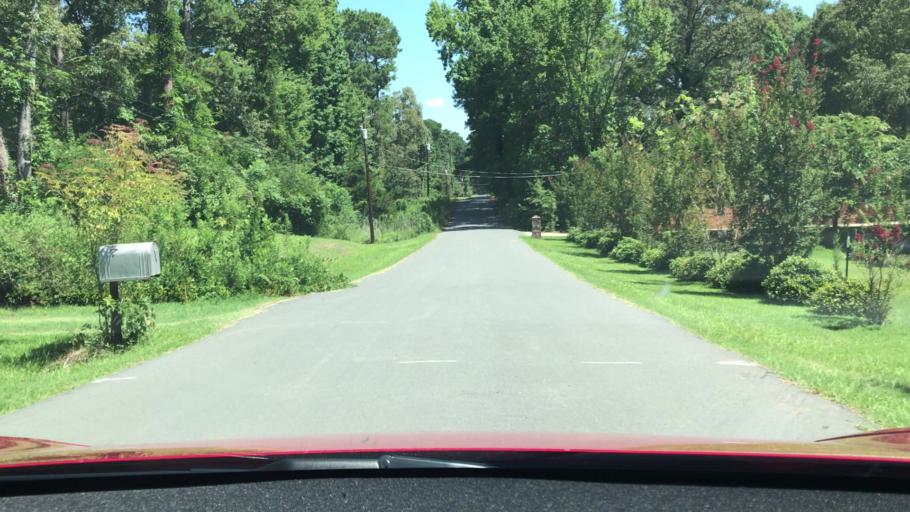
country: US
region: Louisiana
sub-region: De Soto Parish
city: Stonewall
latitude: 32.3416
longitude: -93.7085
